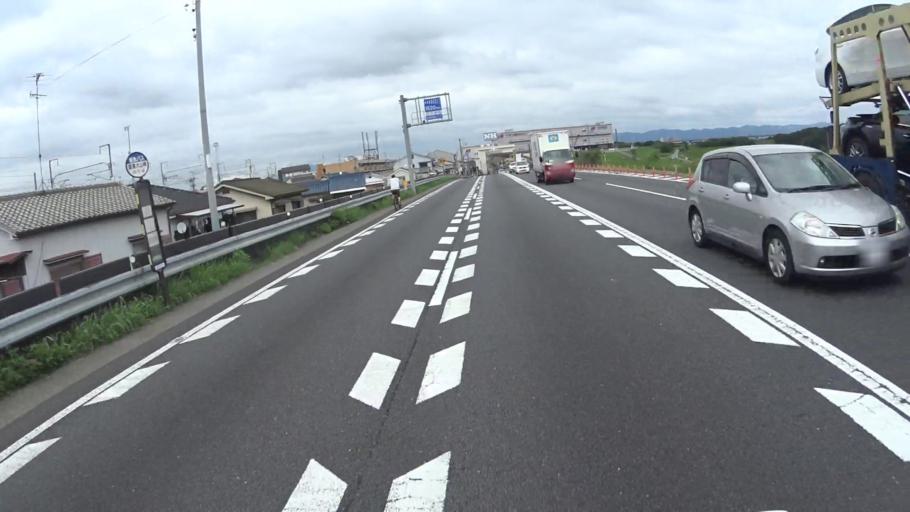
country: JP
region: Kyoto
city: Yawata
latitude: 34.8923
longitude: 135.6833
